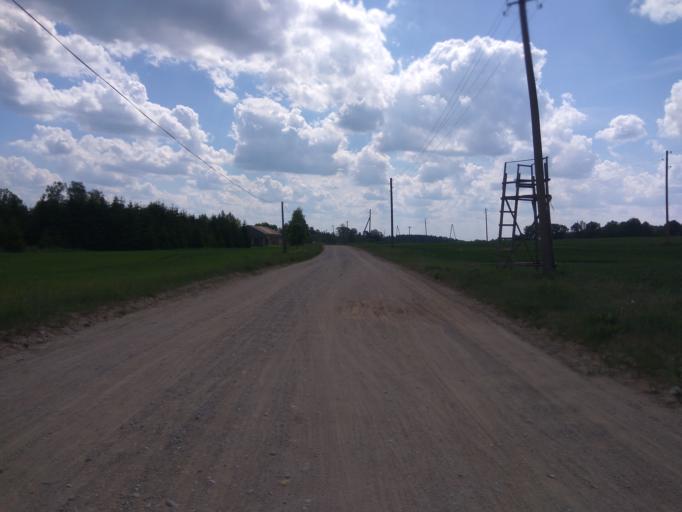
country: LV
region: Kuldigas Rajons
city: Kuldiga
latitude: 56.8959
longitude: 21.9689
